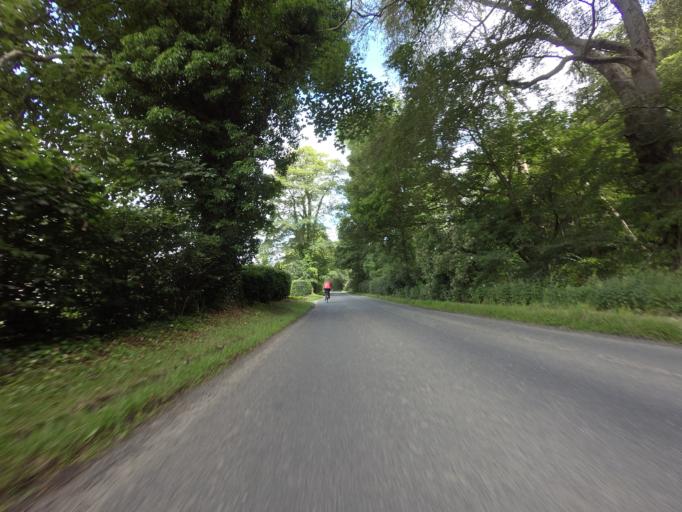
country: GB
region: Scotland
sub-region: Aberdeenshire
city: Turriff
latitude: 57.5512
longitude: -2.4865
